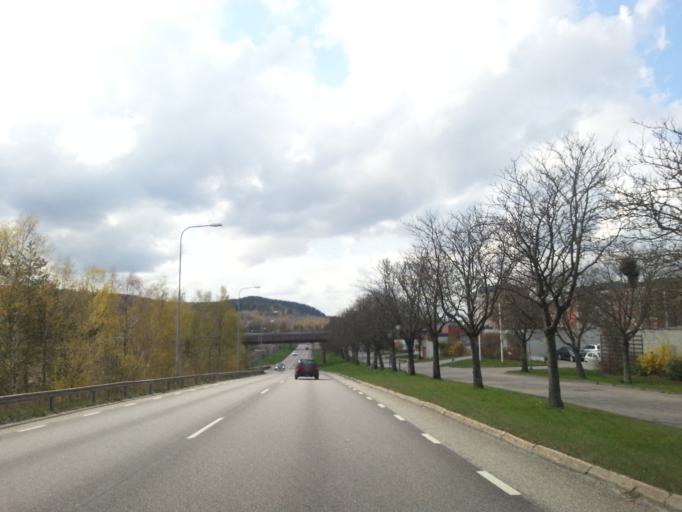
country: SE
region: Vaestra Goetaland
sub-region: Goteborg
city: Hammarkullen
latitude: 57.7718
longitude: 12.0230
